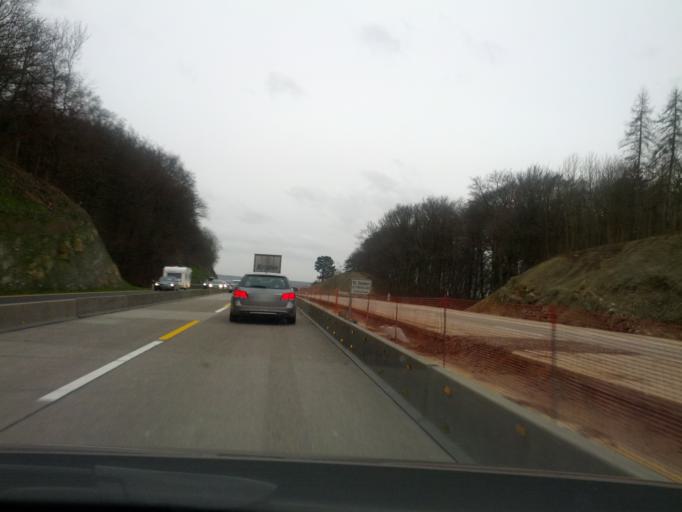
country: DE
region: Lower Saxony
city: Bockenem
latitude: 51.9702
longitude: 10.1458
